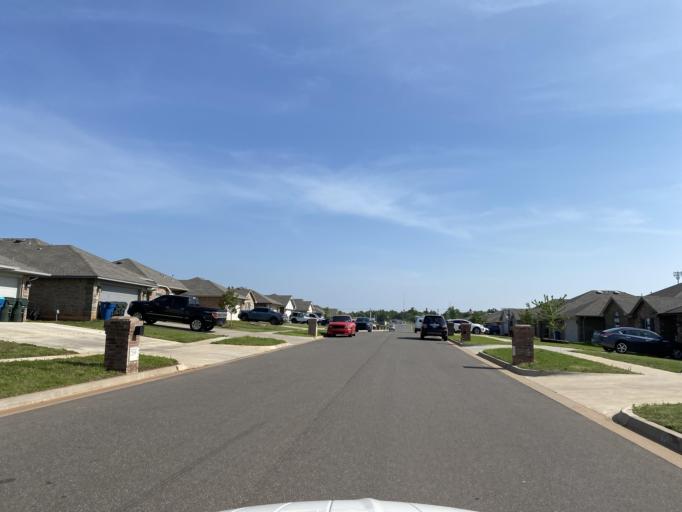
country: US
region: Oklahoma
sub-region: Oklahoma County
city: Nicoma Park
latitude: 35.4382
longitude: -97.3408
